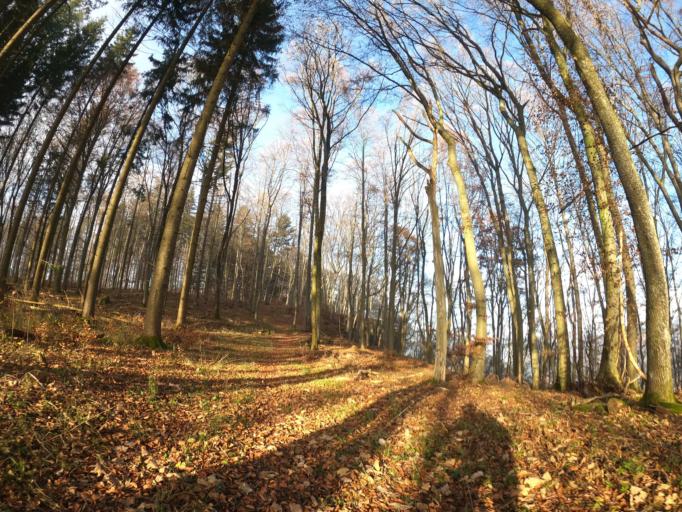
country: DE
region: Baden-Wuerttemberg
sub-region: Regierungsbezirk Stuttgart
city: Deggingen
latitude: 48.5986
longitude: 9.7440
